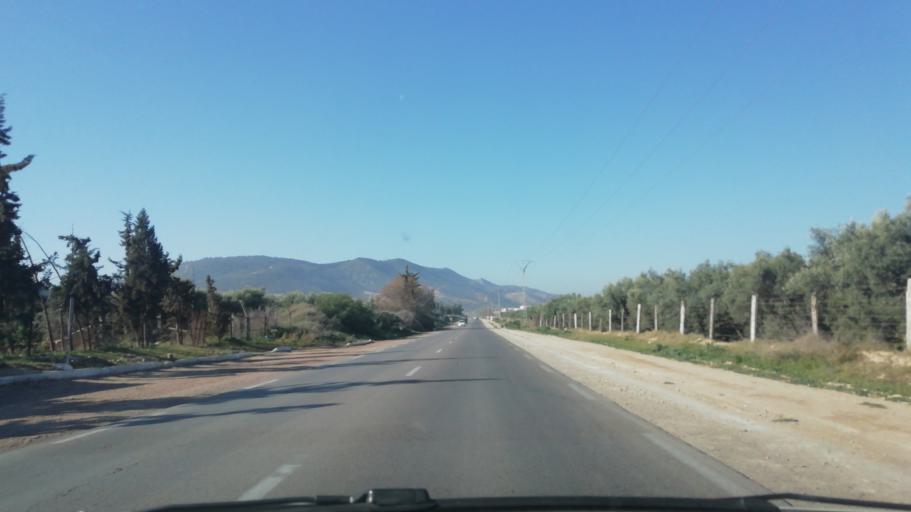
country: DZ
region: Mascara
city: Sig
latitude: 35.5372
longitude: -0.1367
